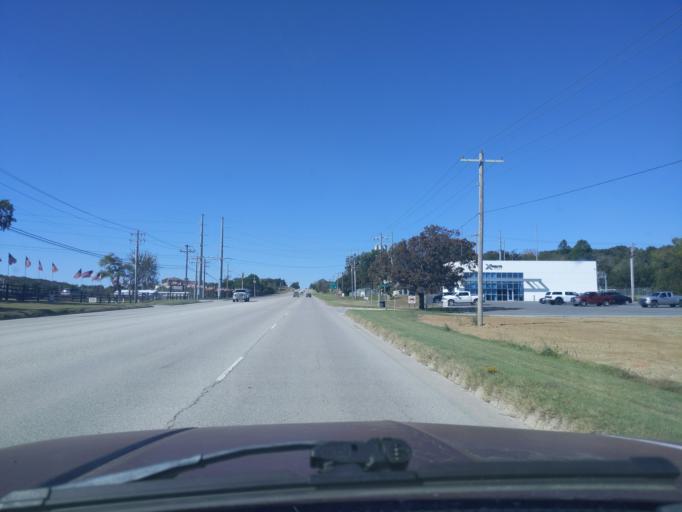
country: US
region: Oklahoma
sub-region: Tulsa County
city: Glenpool
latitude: 35.9885
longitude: -96.0328
